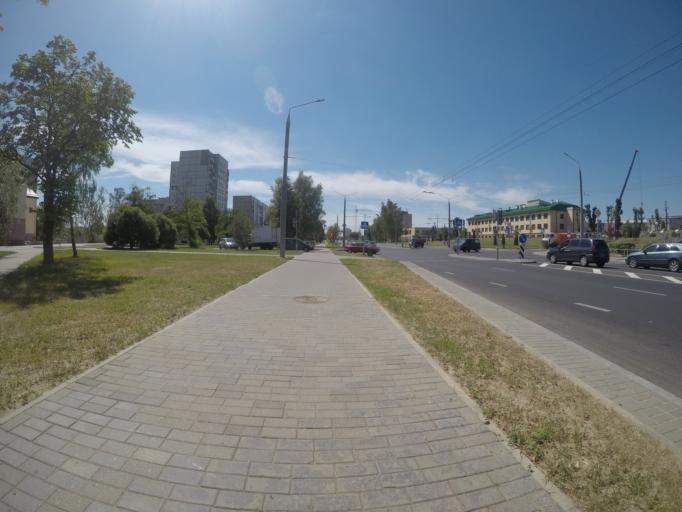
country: BY
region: Grodnenskaya
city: Hrodna
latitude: 53.7048
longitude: 23.8401
